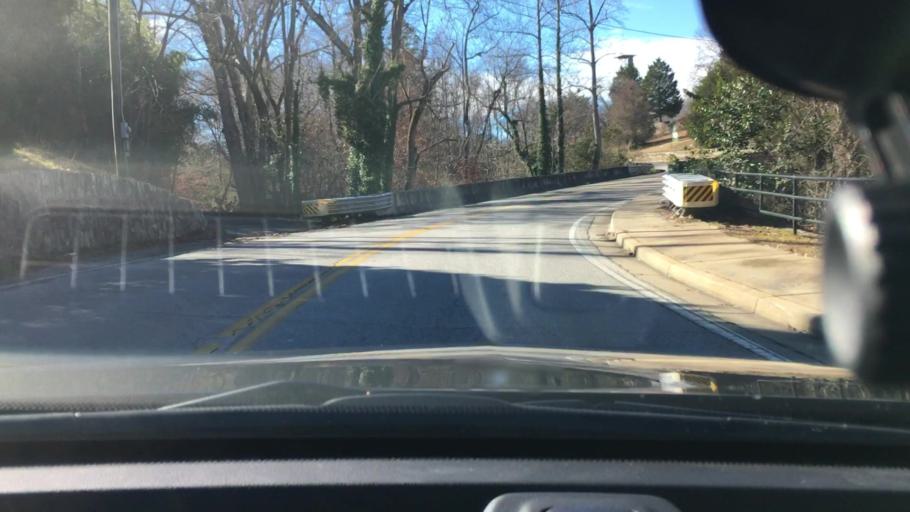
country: US
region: South Carolina
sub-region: Spartanburg County
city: Pacolet
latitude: 34.9194
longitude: -81.7459
